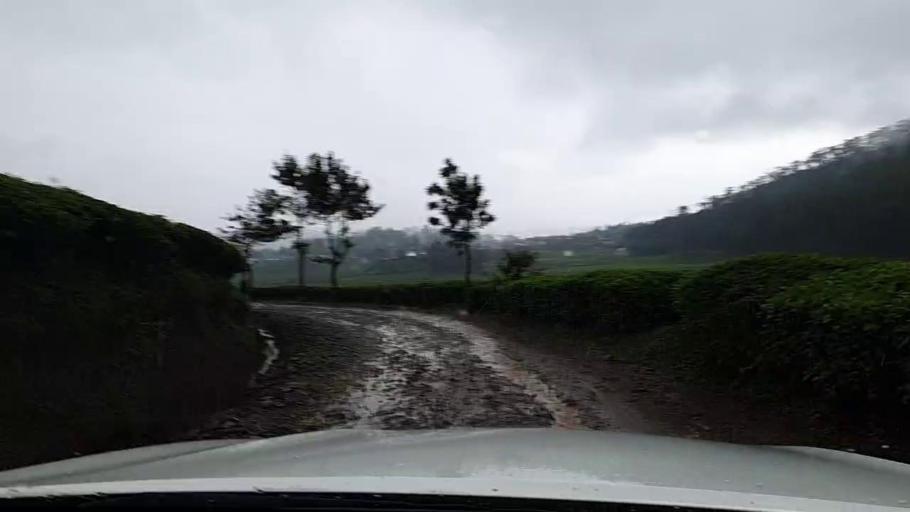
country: RW
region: Western Province
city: Cyangugu
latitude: -2.4571
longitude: 29.0402
